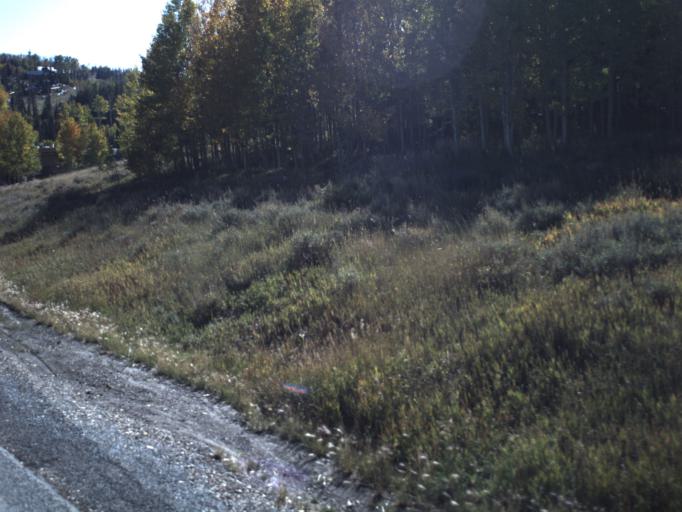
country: US
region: Utah
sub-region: Iron County
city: Parowan
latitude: 37.7044
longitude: -112.8485
